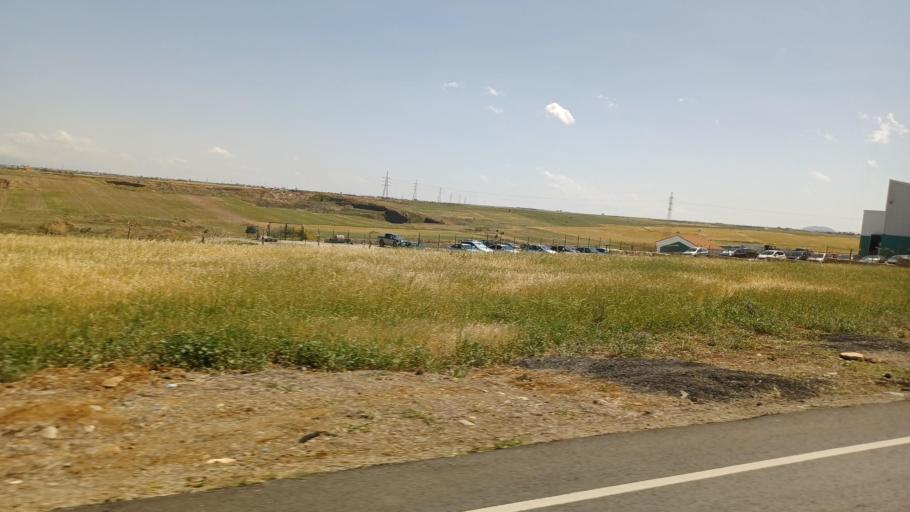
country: CY
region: Lefkosia
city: Astromeritis
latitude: 35.1246
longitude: 33.0133
